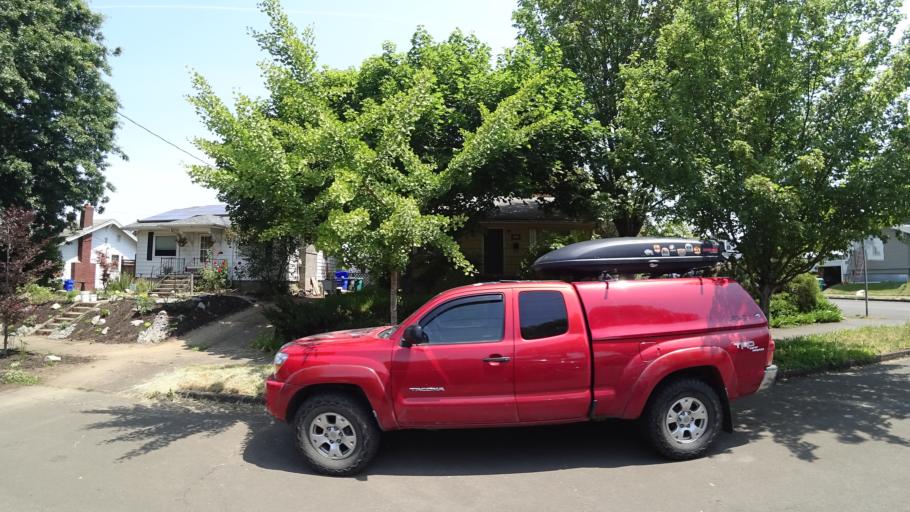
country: US
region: Oregon
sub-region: Multnomah County
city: Portland
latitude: 45.5781
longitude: -122.6723
